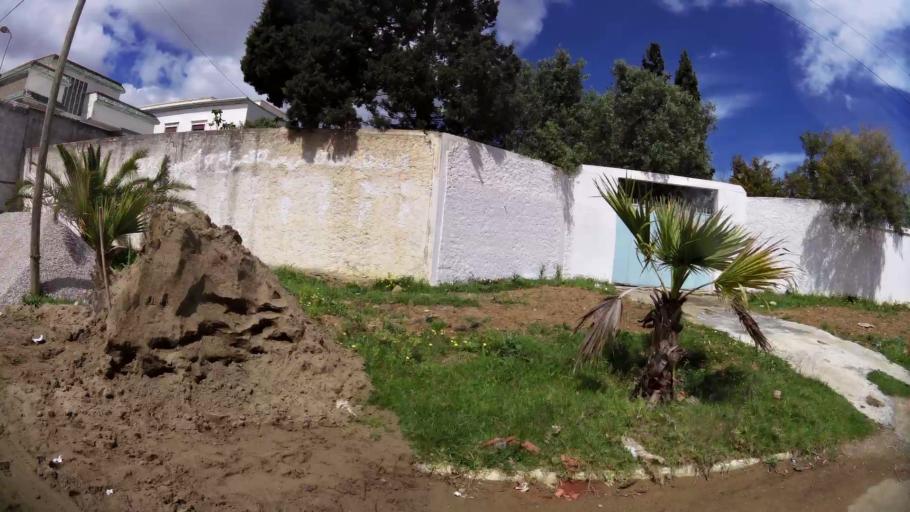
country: MA
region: Tanger-Tetouan
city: Tetouan
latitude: 35.5910
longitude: -5.3422
